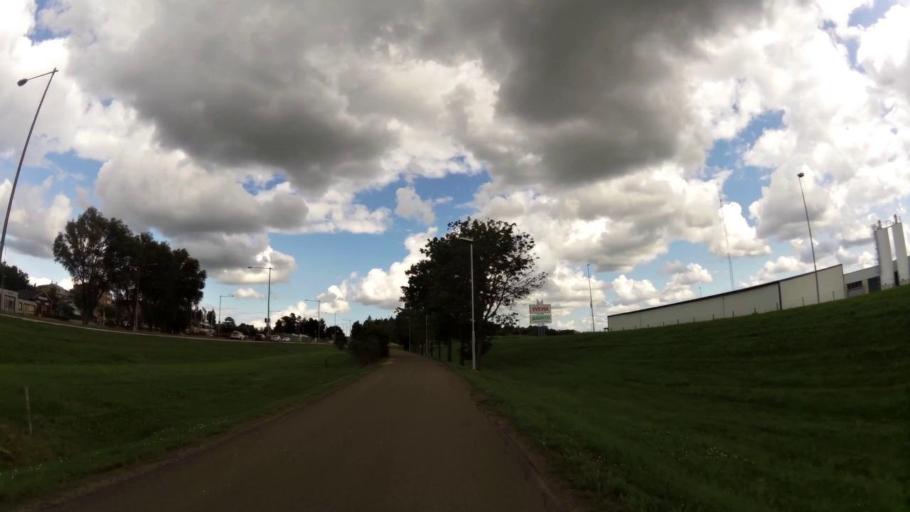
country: SE
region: OEstergoetland
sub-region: Linkopings Kommun
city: Linkoping
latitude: 58.4253
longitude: 15.6759
